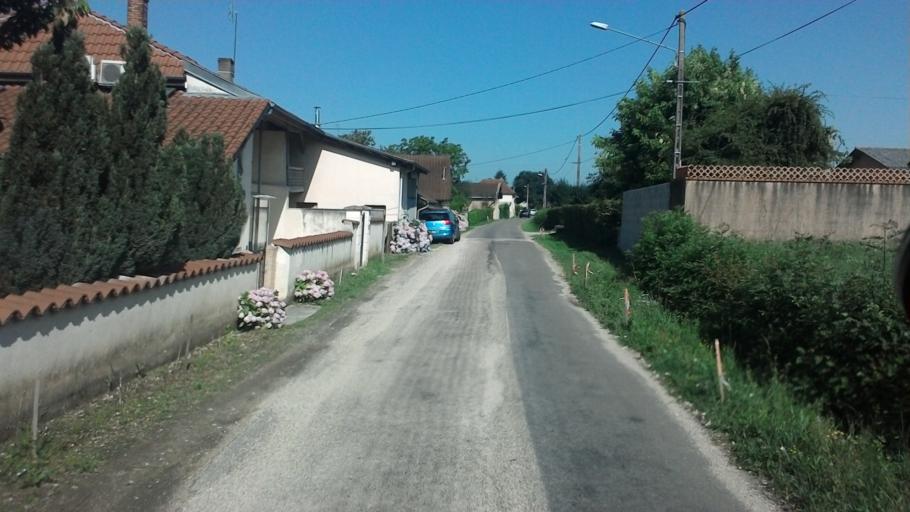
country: FR
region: Rhone-Alpes
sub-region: Departement de l'Ain
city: Montrevel-en-Bresse
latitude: 46.4017
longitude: 5.1134
